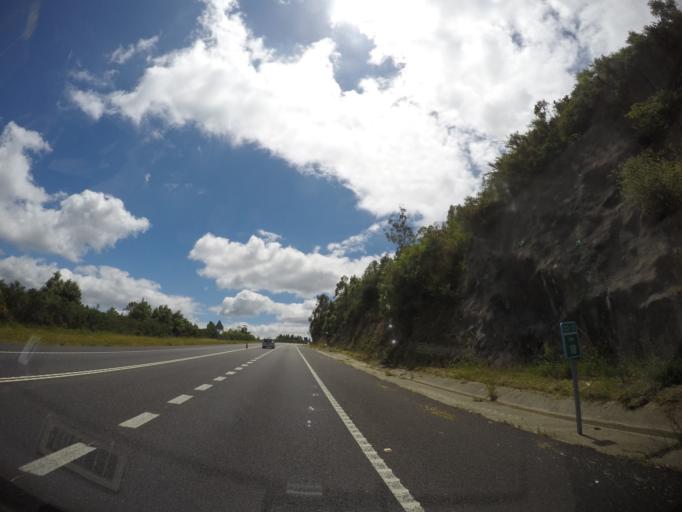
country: ES
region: Aragon
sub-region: Provincia de Zaragoza
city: El Burgo de Ebro
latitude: 41.5241
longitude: -0.7063
